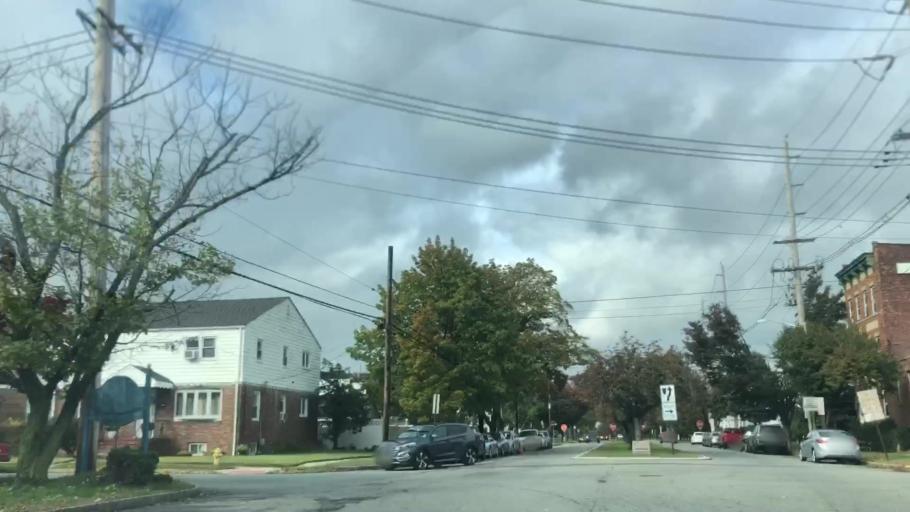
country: US
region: New Jersey
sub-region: Essex County
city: Bloomfield
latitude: 40.7865
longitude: -74.1819
